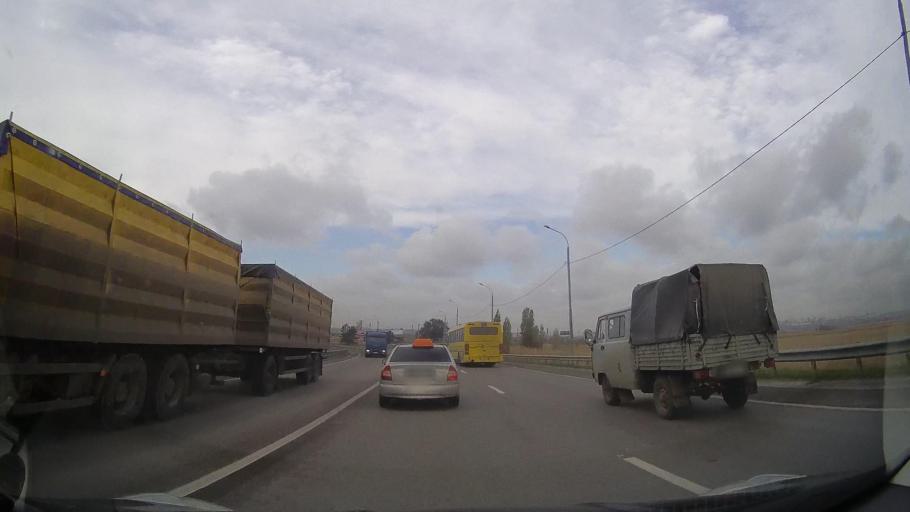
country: RU
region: Rostov
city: Bataysk
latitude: 47.1720
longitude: 39.7463
